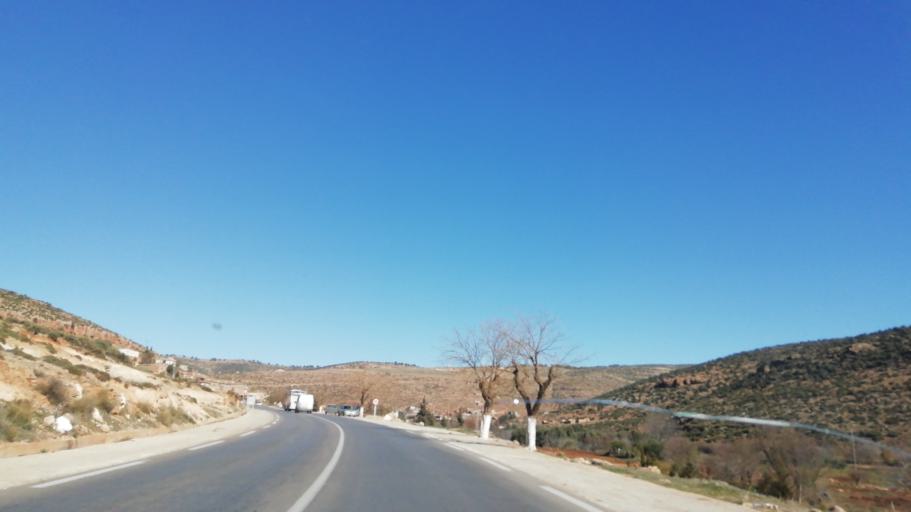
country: DZ
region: Tlemcen
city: Sebdou
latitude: 34.6896
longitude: -1.3146
